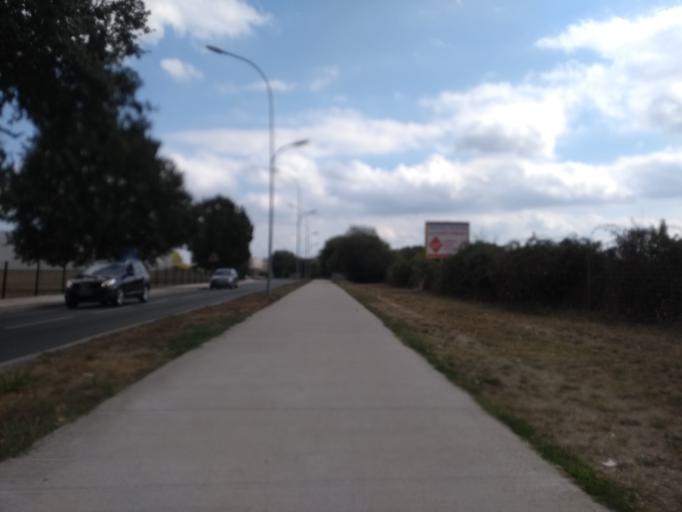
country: FR
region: Aquitaine
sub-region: Departement de la Gironde
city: Talence
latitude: 44.7964
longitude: -0.5791
